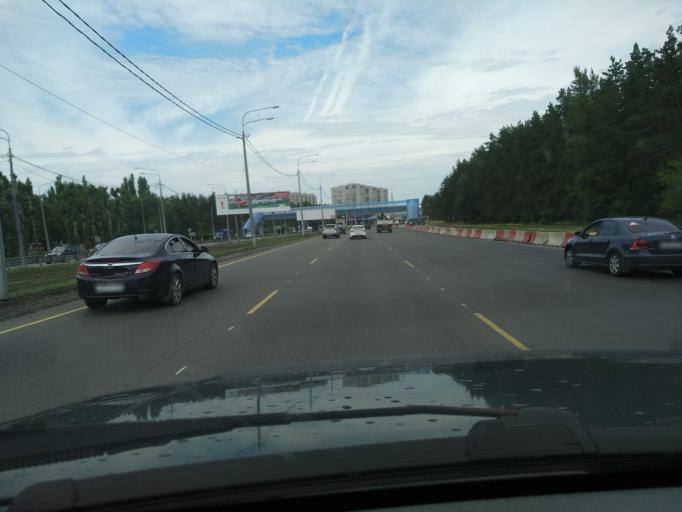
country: RU
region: Voronezj
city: Podgornoye
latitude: 51.7266
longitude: 39.1791
